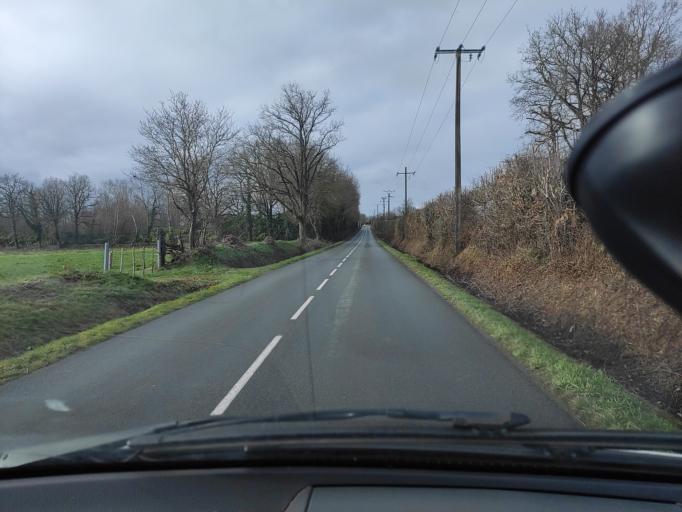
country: FR
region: Pays de la Loire
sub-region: Departement de la Vendee
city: La Boissiere-des-Landes
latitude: 46.5685
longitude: -1.4850
